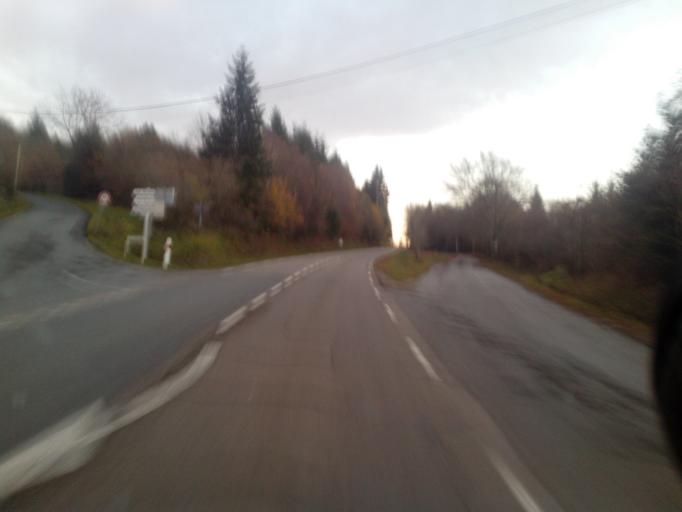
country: FR
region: Limousin
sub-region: Departement de la Correze
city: Meymac
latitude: 45.5282
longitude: 2.1590
